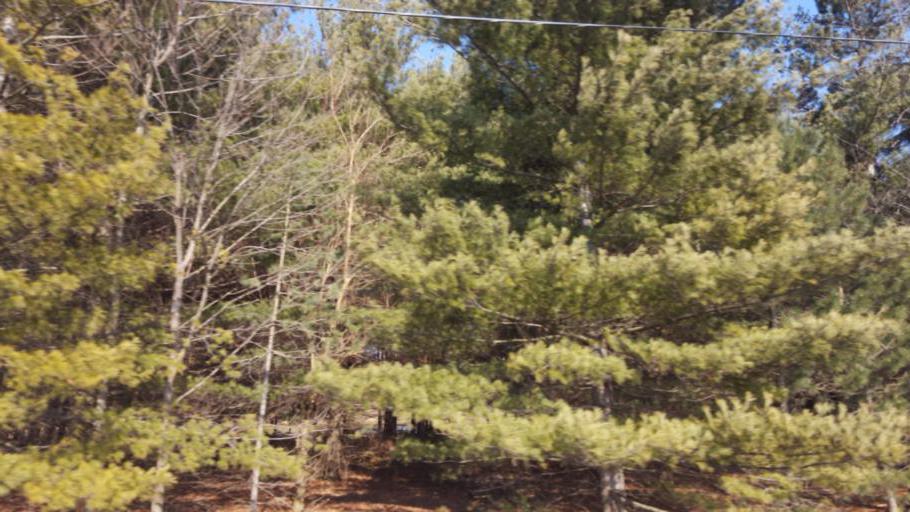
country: US
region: Ohio
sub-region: Richland County
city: Shelby
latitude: 40.8577
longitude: -82.5904
